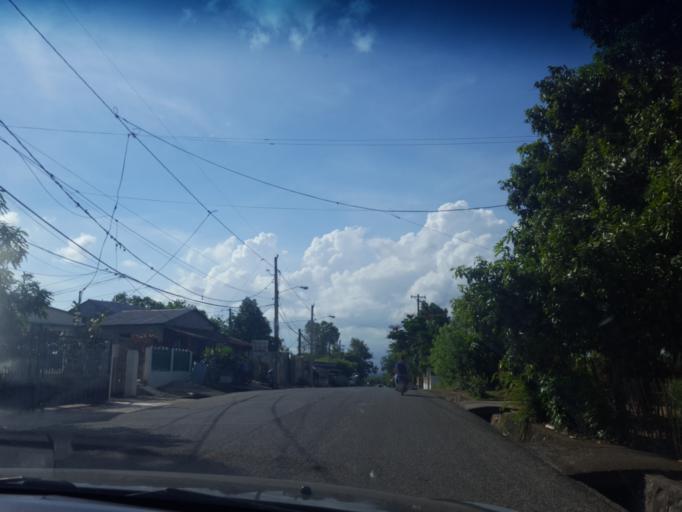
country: DO
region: Santiago
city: Licey al Medio
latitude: 19.3688
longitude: -70.6067
